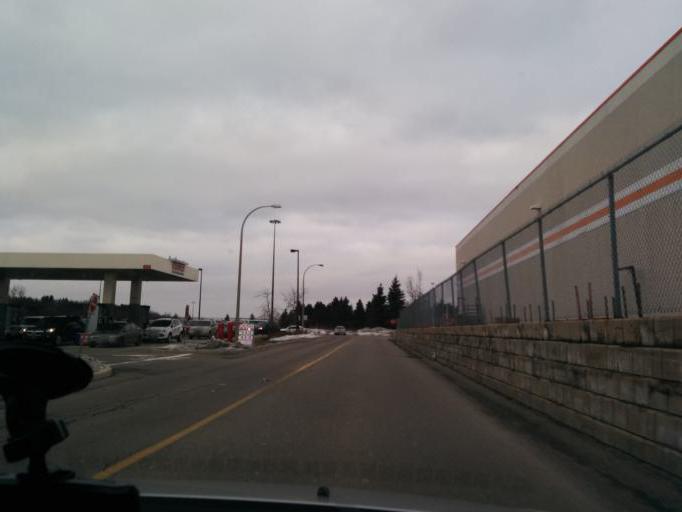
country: CA
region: Ontario
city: Ancaster
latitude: 43.2302
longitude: -79.9456
